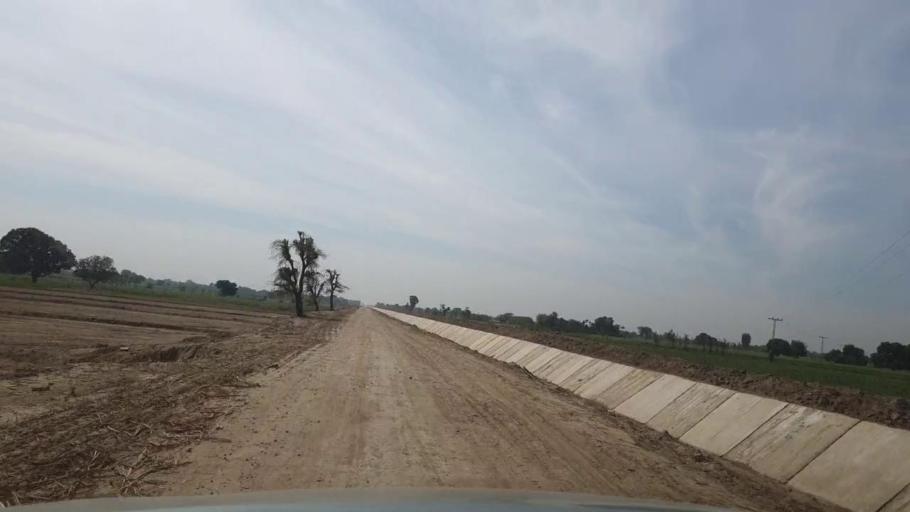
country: PK
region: Sindh
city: Kunri
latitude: 25.1565
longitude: 69.5893
